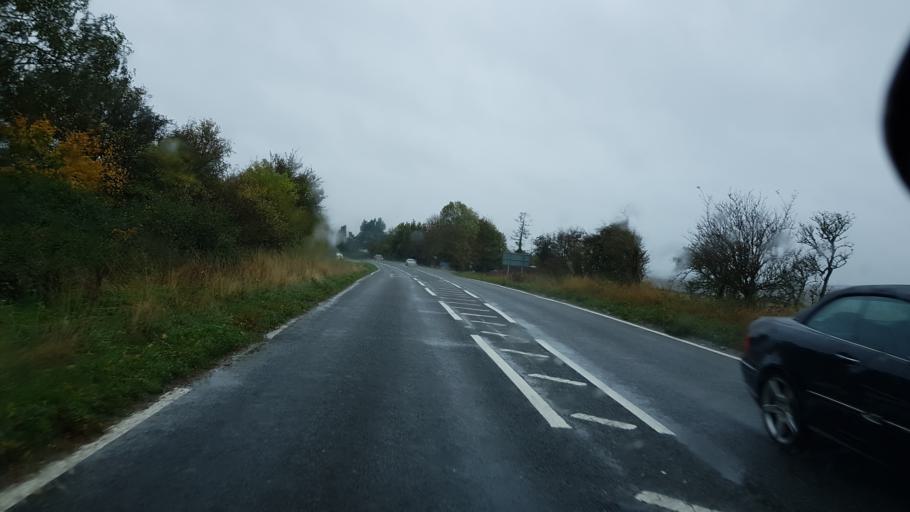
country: GB
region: England
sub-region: Oxfordshire
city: Burford
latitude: 51.7967
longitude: -1.6088
